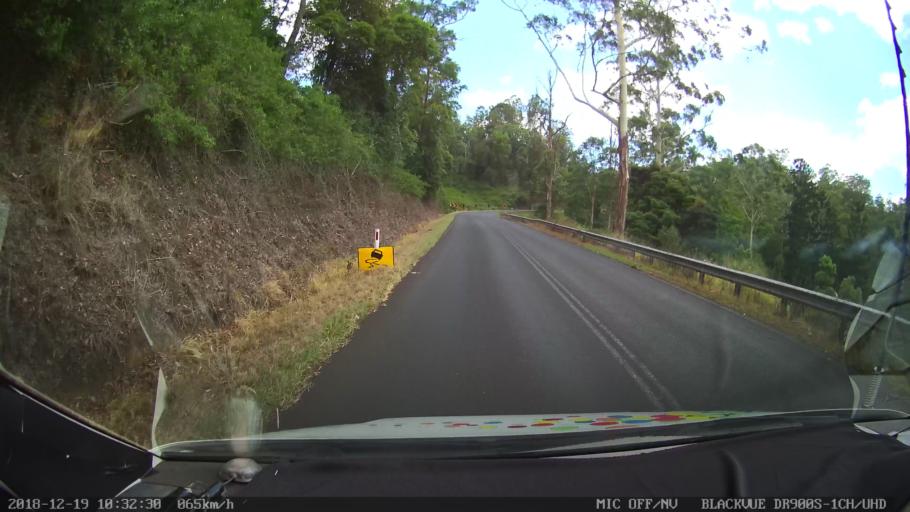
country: AU
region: New South Wales
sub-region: Lismore Municipality
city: Larnook
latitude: -28.5811
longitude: 153.1215
